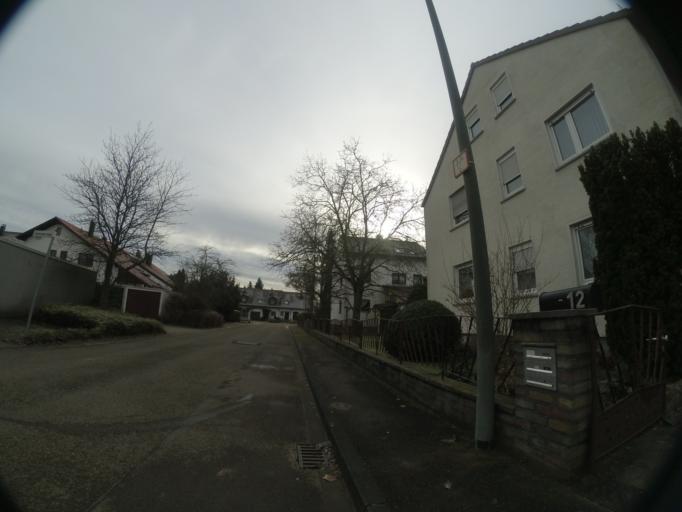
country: DE
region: Bavaria
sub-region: Swabia
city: Neu-Ulm
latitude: 48.4091
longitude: 10.0466
